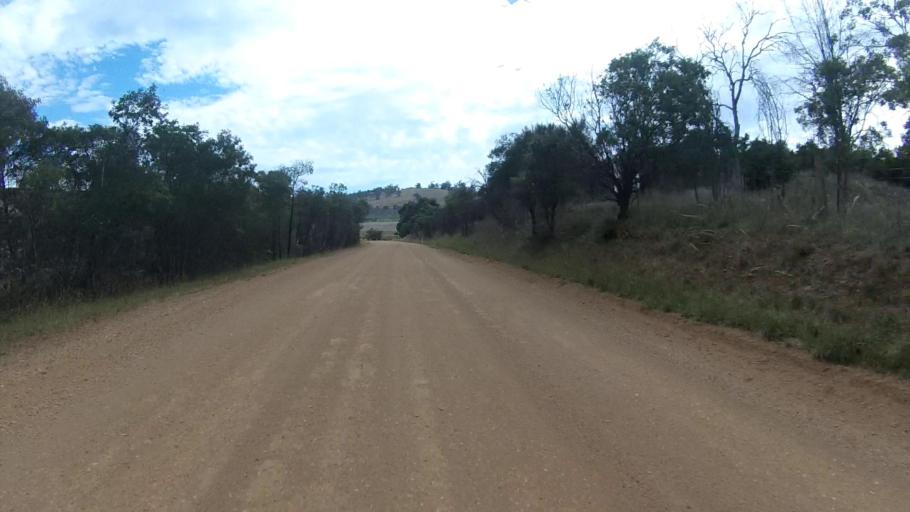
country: AU
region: Tasmania
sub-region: Sorell
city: Sorell
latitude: -42.6971
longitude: 147.4626
